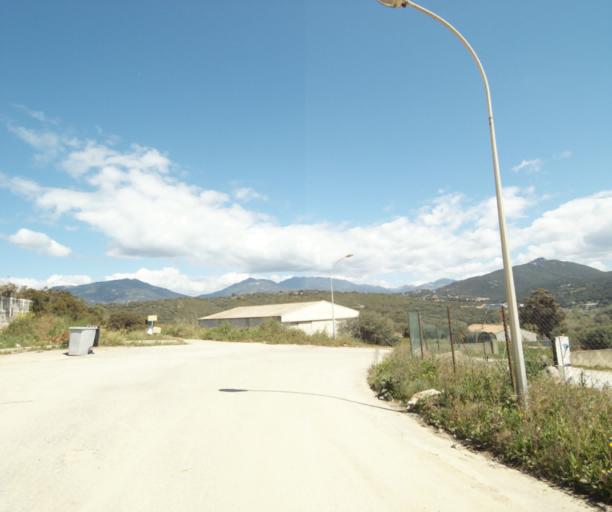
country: FR
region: Corsica
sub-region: Departement de la Corse-du-Sud
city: Propriano
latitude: 41.6560
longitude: 8.8993
